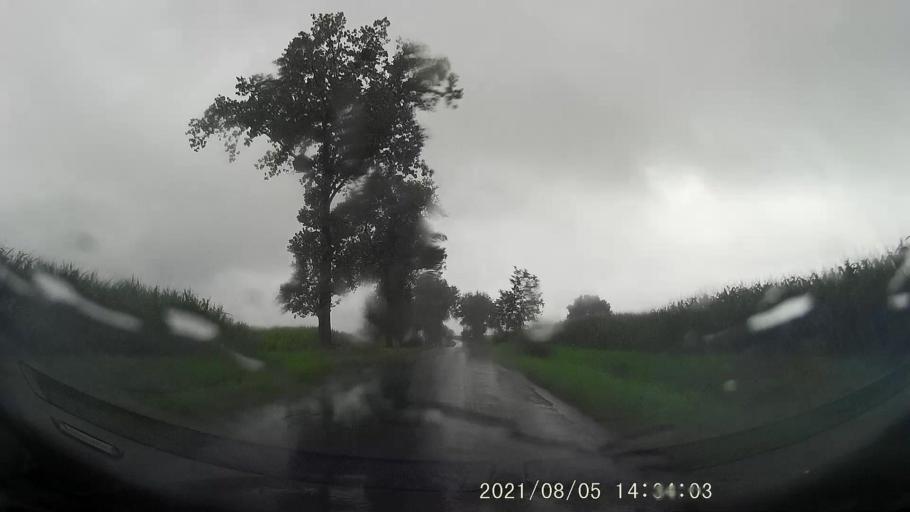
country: PL
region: Opole Voivodeship
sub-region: Powiat nyski
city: Korfantow
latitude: 50.4684
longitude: 17.5261
